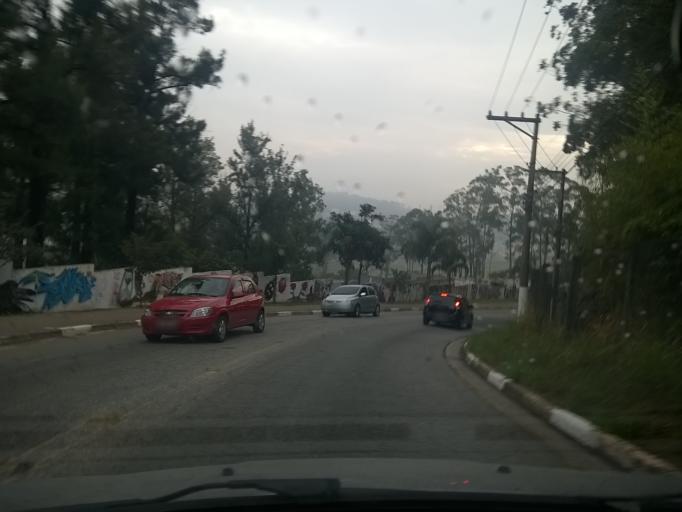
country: BR
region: Sao Paulo
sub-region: Caieiras
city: Caieiras
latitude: -23.3935
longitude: -46.7417
